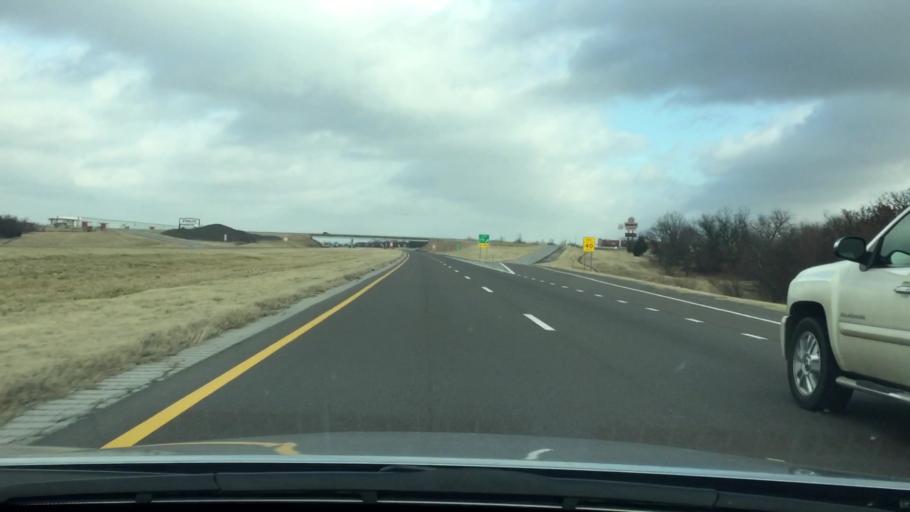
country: US
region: Oklahoma
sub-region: Garvin County
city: Maysville
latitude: 34.8219
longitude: -97.3079
